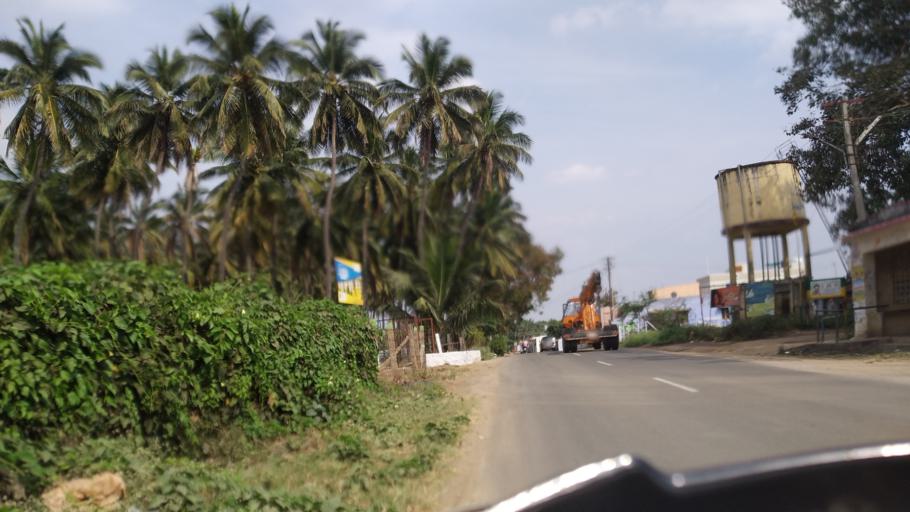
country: IN
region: Tamil Nadu
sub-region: Coimbatore
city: Perur
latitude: 10.9578
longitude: 76.7572
